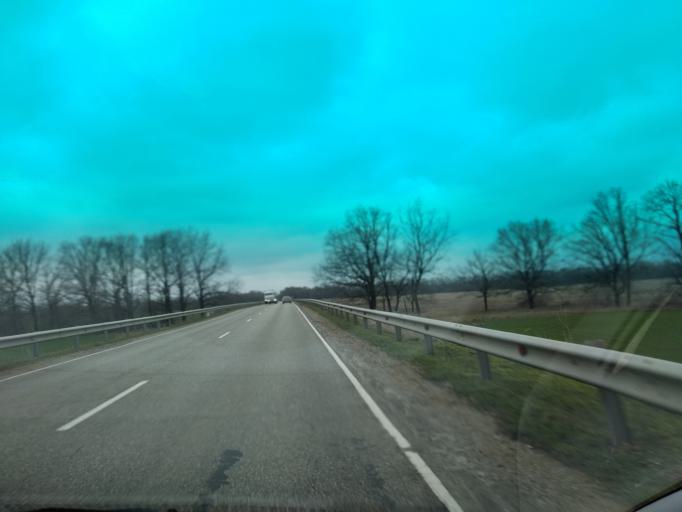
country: RU
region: Krasnodarskiy
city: Novorozhdestvenskaya
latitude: 45.7681
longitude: 39.9480
